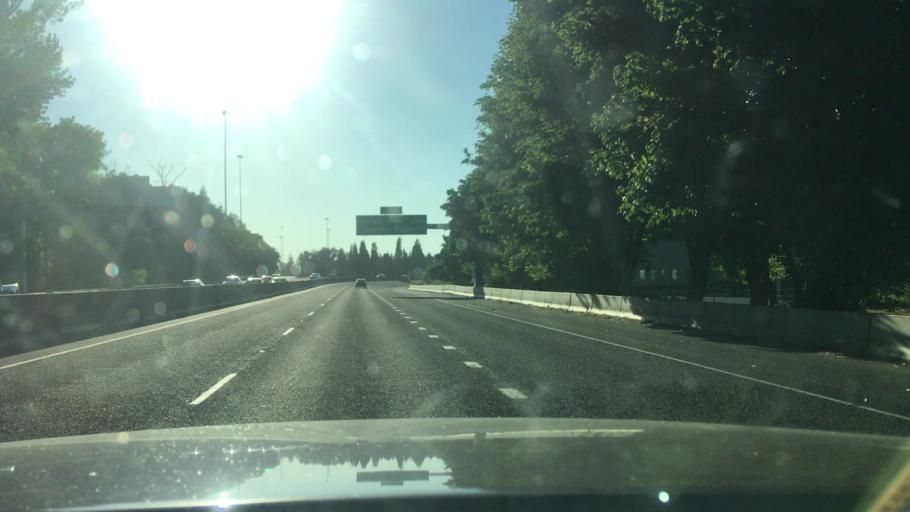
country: US
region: Oregon
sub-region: Lane County
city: Eugene
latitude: 44.0626
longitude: -123.0925
